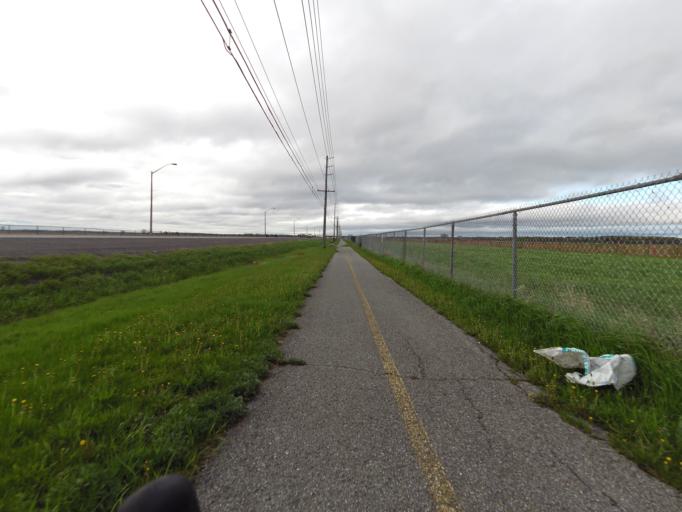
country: CA
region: Ontario
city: Bells Corners
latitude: 45.3122
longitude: -75.7713
